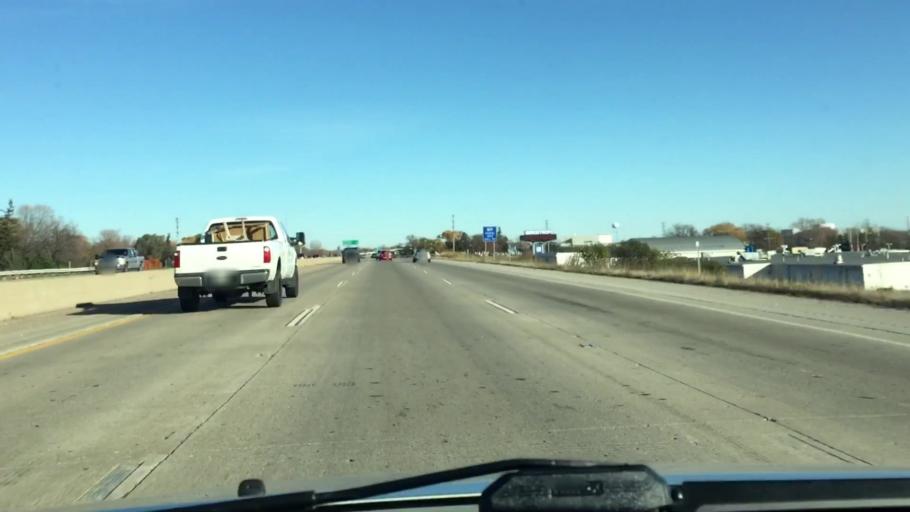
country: US
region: Wisconsin
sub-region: Winnebago County
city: Neenah
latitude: 44.1902
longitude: -88.4874
